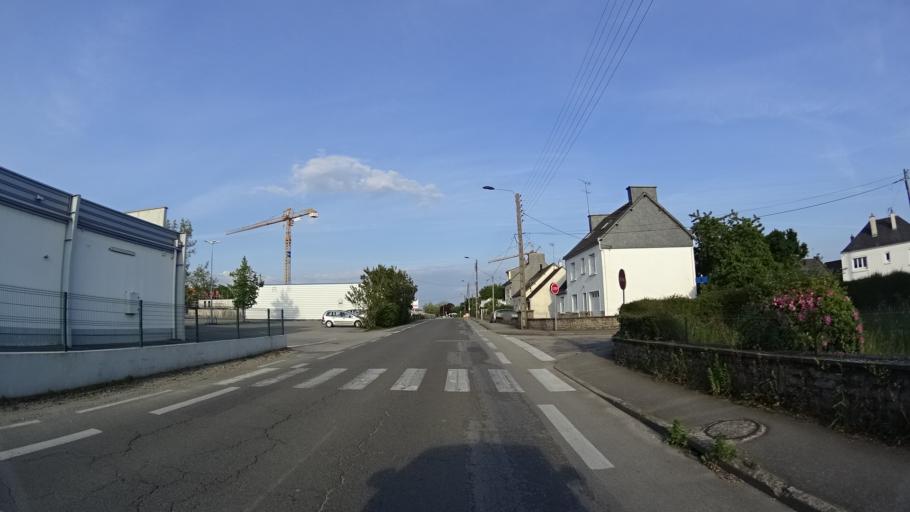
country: FR
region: Brittany
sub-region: Departement du Morbihan
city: Vannes
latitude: 47.6517
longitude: -2.7317
